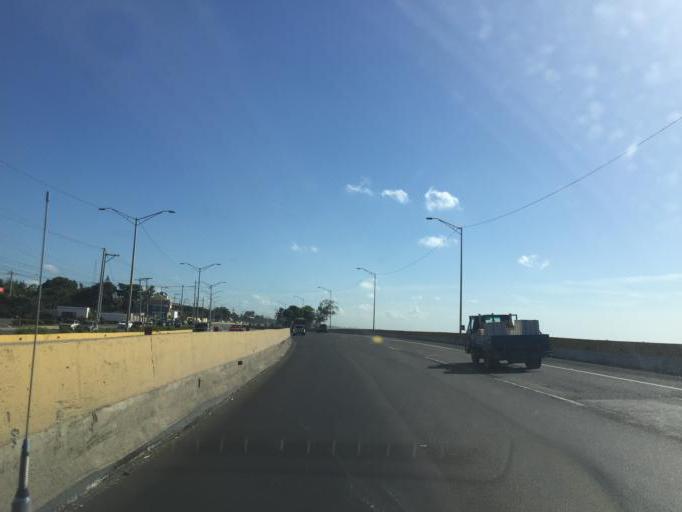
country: DO
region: Santo Domingo
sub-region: Santo Domingo
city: Santo Domingo Este
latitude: 18.4644
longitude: -69.8097
